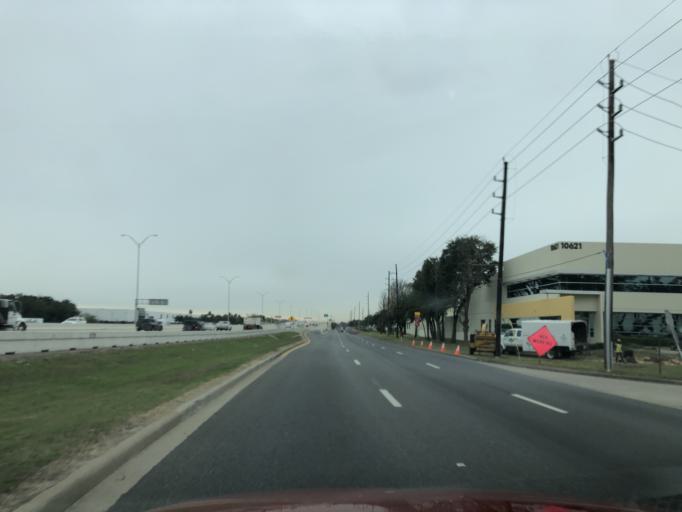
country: US
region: Texas
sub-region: Fort Bend County
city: Missouri City
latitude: 29.6422
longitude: -95.5374
